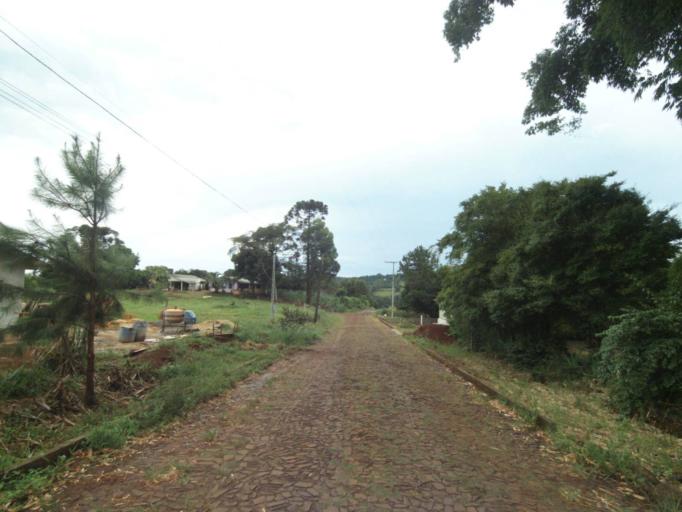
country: BR
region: Parana
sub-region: Guaraniacu
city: Guaraniacu
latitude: -25.0942
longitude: -52.8658
